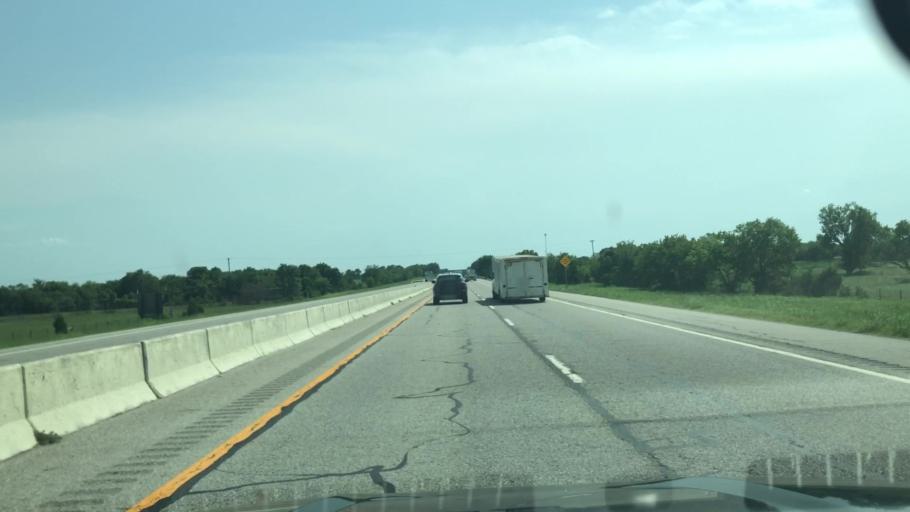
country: US
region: Oklahoma
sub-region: Ottawa County
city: Fairland
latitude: 36.7891
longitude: -94.8859
